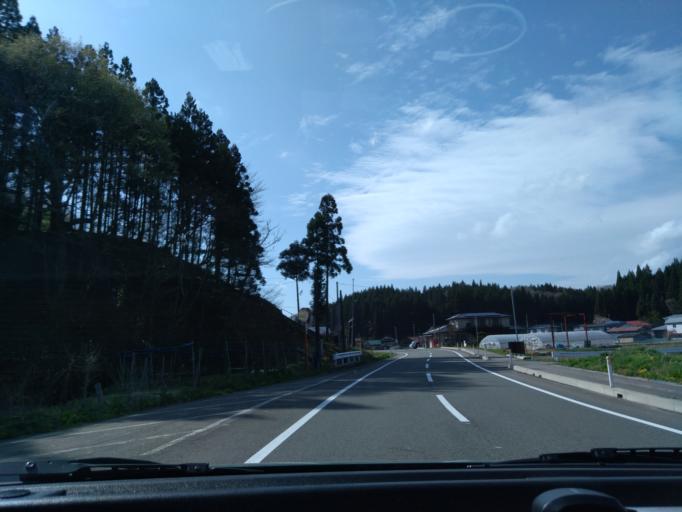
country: JP
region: Akita
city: Akita
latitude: 39.7133
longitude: 140.1995
